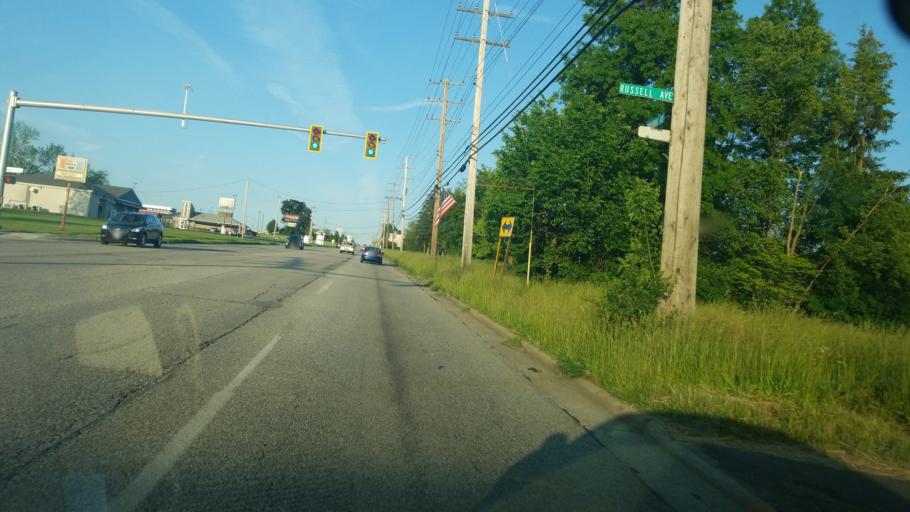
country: US
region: Ohio
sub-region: Mahoning County
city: Austintown
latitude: 41.0995
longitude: -80.7850
